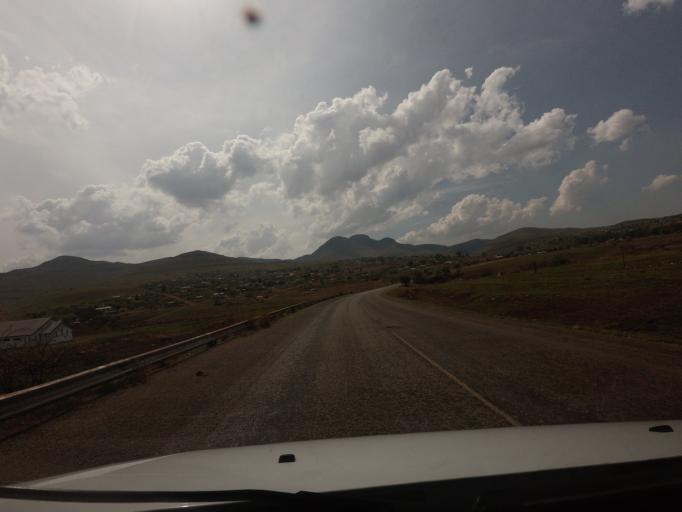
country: ZA
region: Mpumalanga
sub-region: Ehlanzeni District
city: Graksop
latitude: -24.6794
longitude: 30.8046
